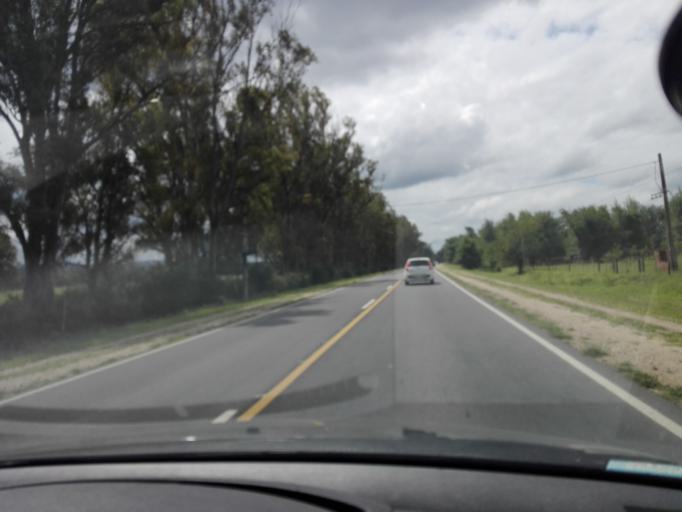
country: AR
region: Cordoba
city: Alta Gracia
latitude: -31.6034
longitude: -64.4491
